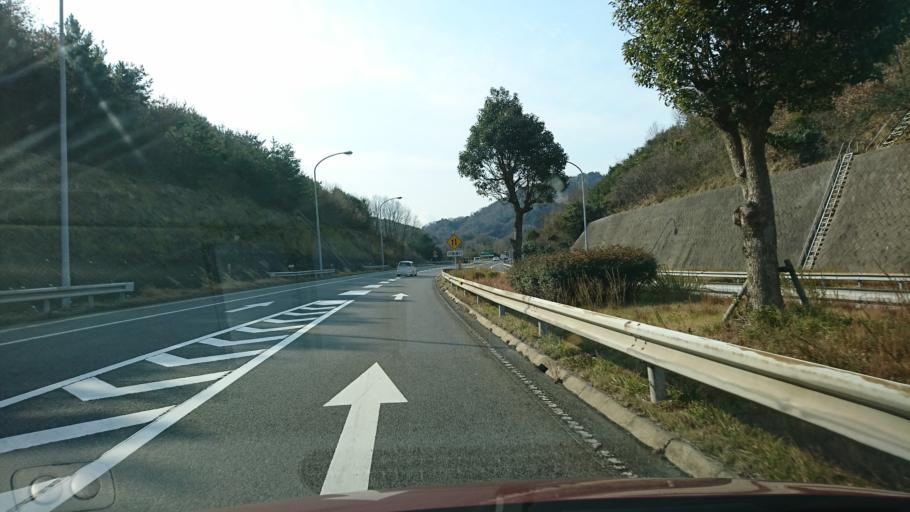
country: JP
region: Hiroshima
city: Innoshima
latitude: 34.3511
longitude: 133.1690
